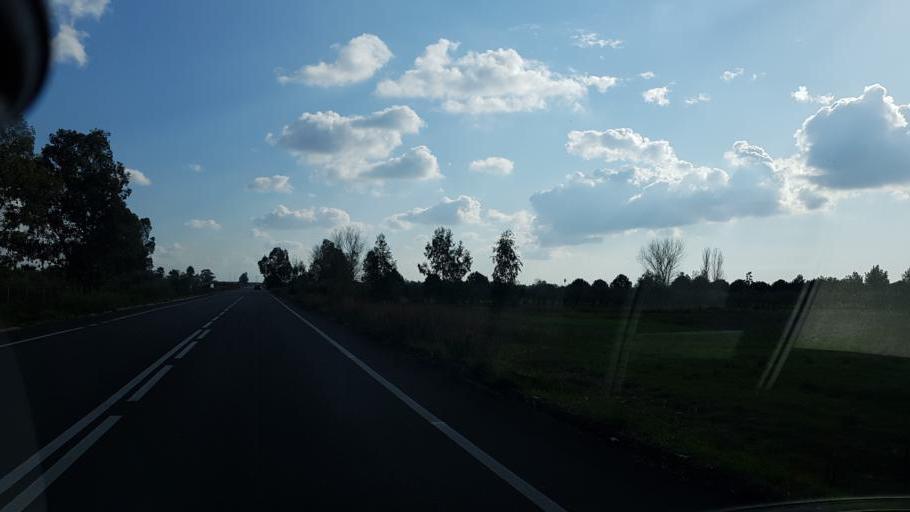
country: IT
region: Apulia
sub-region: Provincia di Lecce
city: Veglie
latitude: 40.3449
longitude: 17.9760
